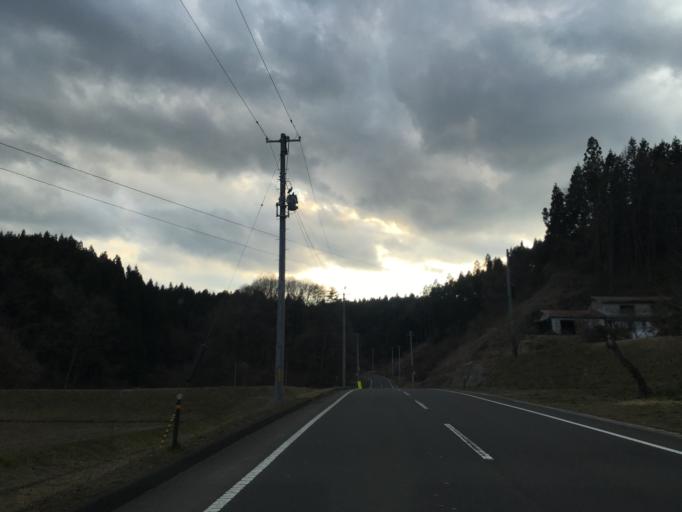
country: JP
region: Fukushima
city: Ishikawa
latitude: 37.0517
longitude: 140.5072
